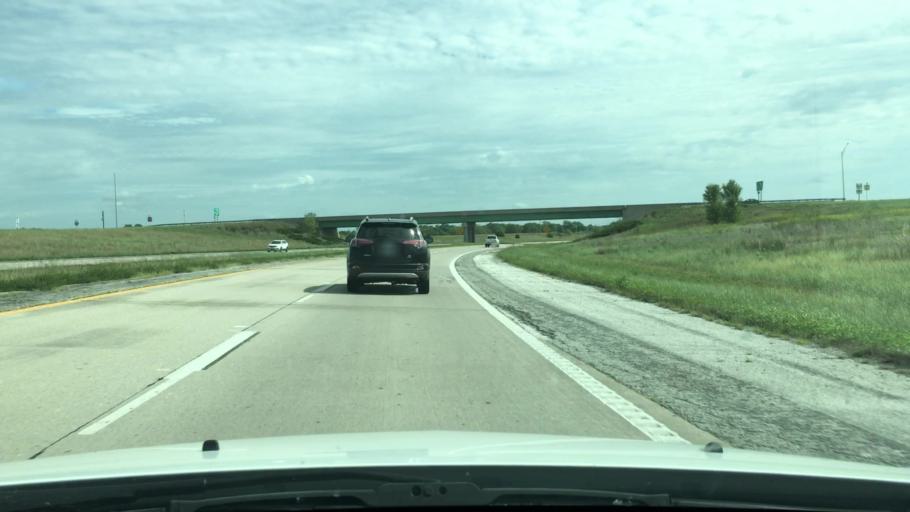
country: US
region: Missouri
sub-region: Audrain County
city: Mexico
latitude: 39.1159
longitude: -91.8932
